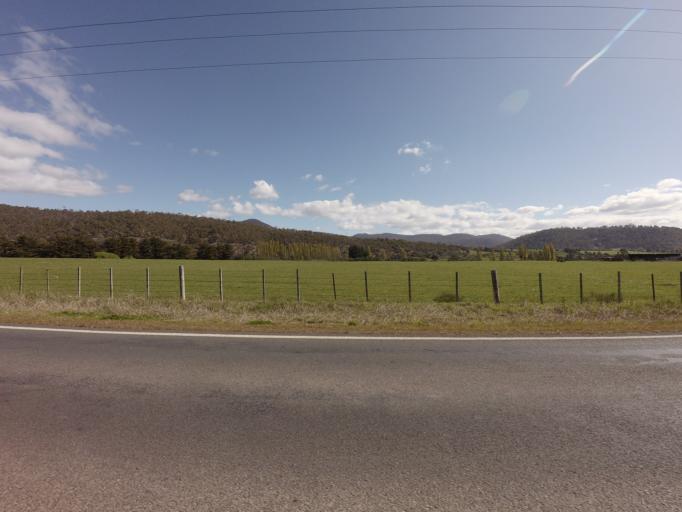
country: AU
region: Tasmania
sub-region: Derwent Valley
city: New Norfolk
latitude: -42.7747
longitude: 147.0359
